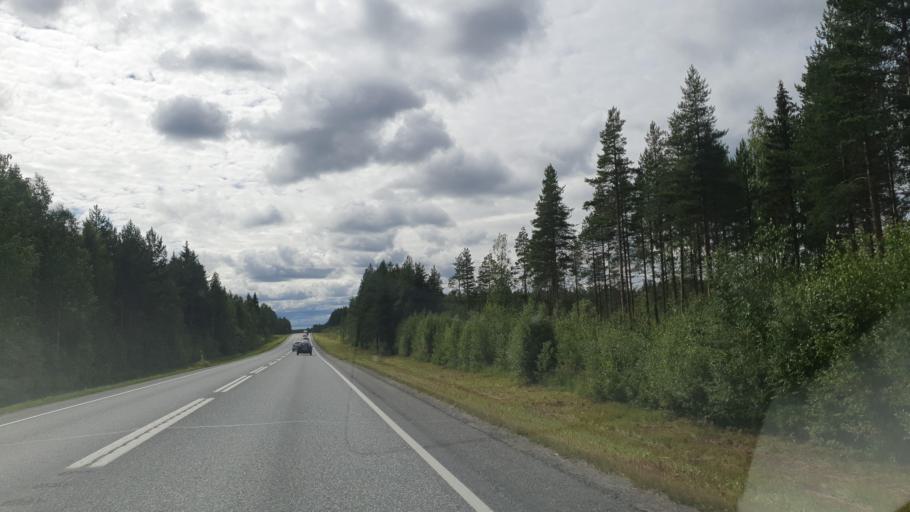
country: FI
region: Kainuu
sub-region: Kajaani
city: Kajaani
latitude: 64.1725
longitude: 27.5503
